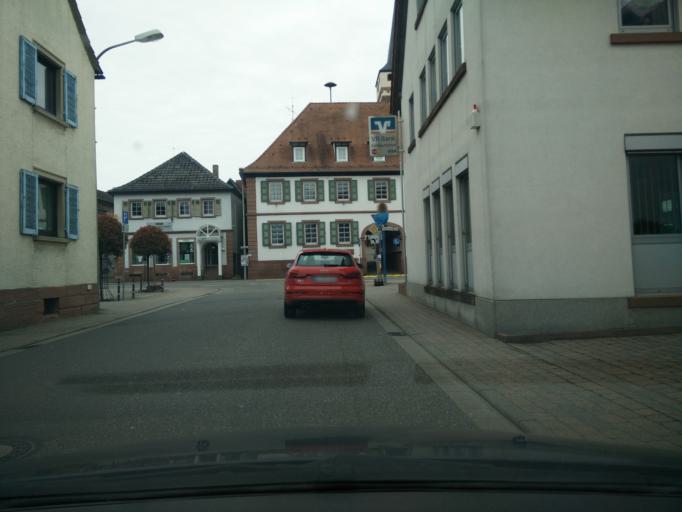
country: DE
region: Rheinland-Pfalz
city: Vollmersweiler
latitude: 49.0593
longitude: 8.0836
